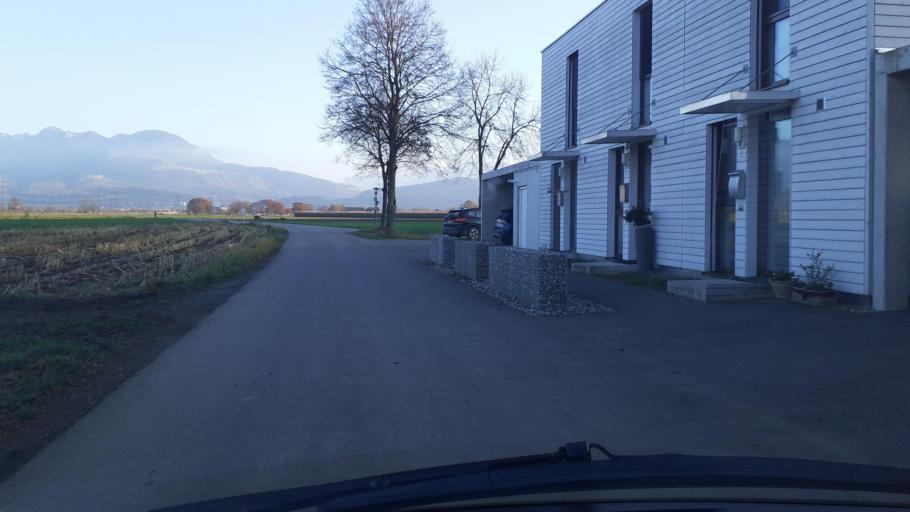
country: AT
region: Vorarlberg
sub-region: Politischer Bezirk Feldkirch
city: Meiningen
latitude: 47.2965
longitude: 9.5895
